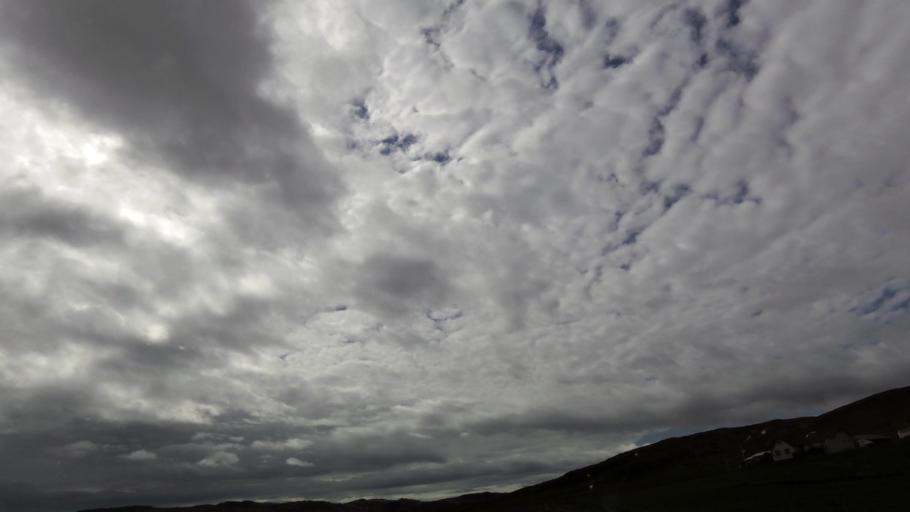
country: IS
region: West
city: Stykkisholmur
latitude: 65.5379
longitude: -22.0612
